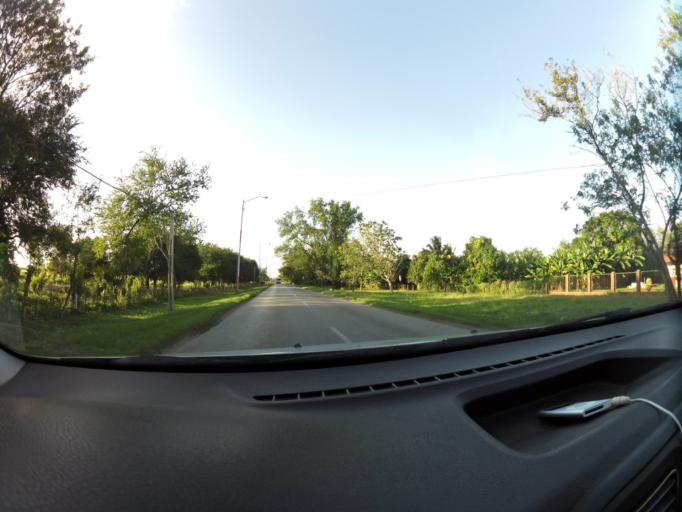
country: CU
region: Granma
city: Bayamo
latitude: 20.3693
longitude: -76.6613
